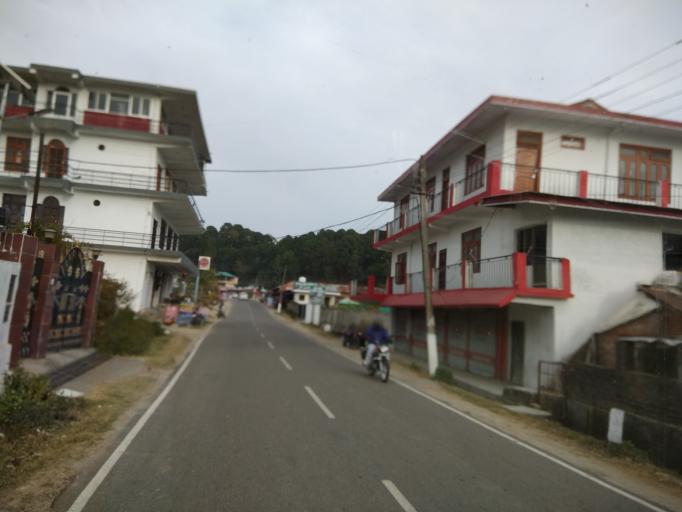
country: IN
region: Himachal Pradesh
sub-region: Kangra
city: Palampur
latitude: 32.1114
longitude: 76.5032
